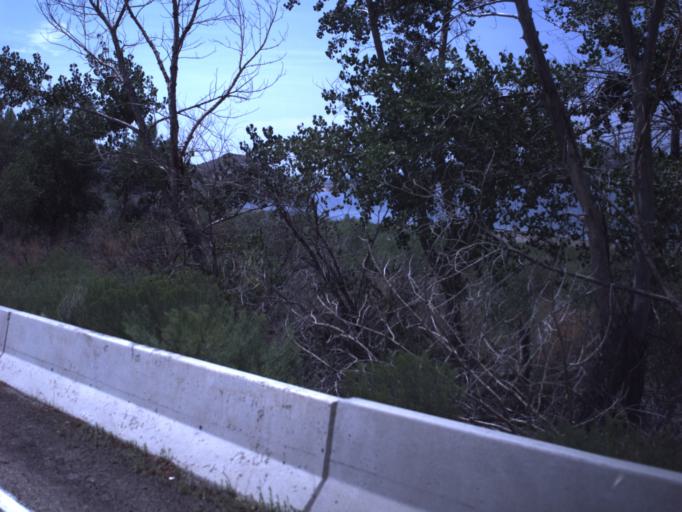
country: US
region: Utah
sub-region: Uintah County
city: Vernal
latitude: 40.5251
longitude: -109.5217
